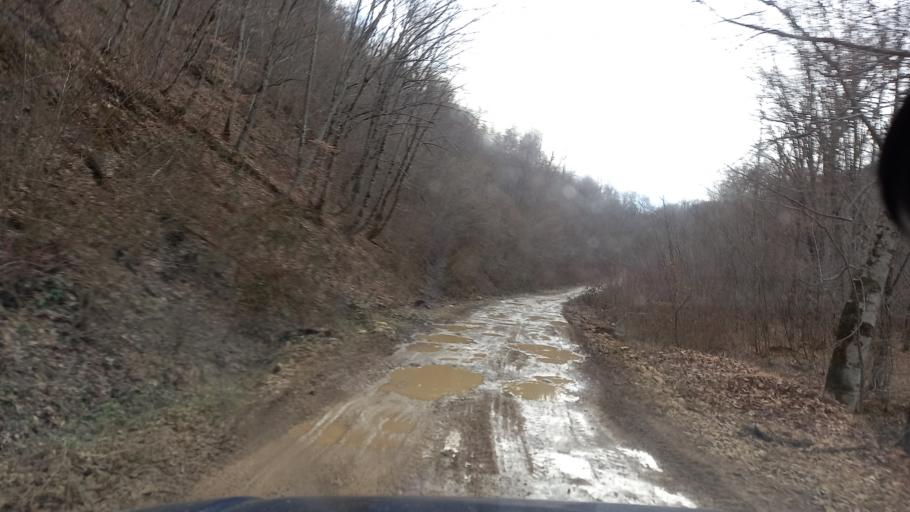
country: RU
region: Adygeya
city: Kamennomostskiy
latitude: 44.1742
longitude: 40.3002
